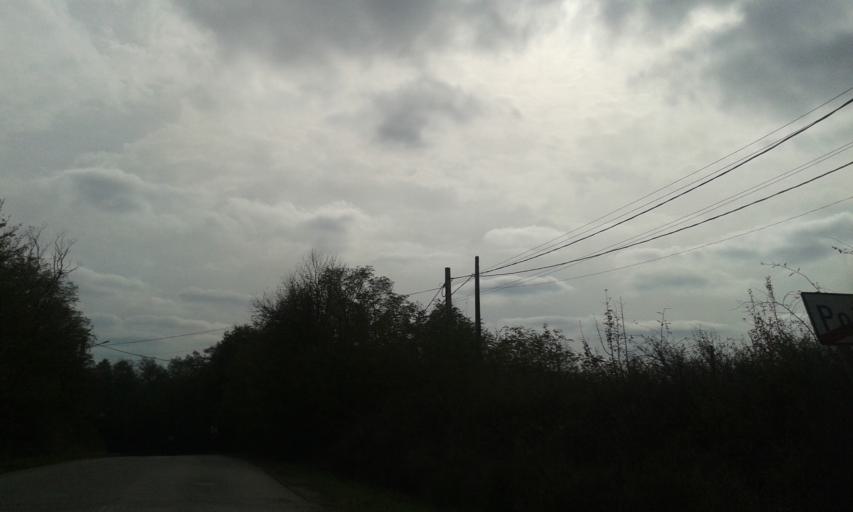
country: RO
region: Gorj
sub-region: Comuna Targu Carbunesti
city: Pojogeni
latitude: 44.9873
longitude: 23.4968
